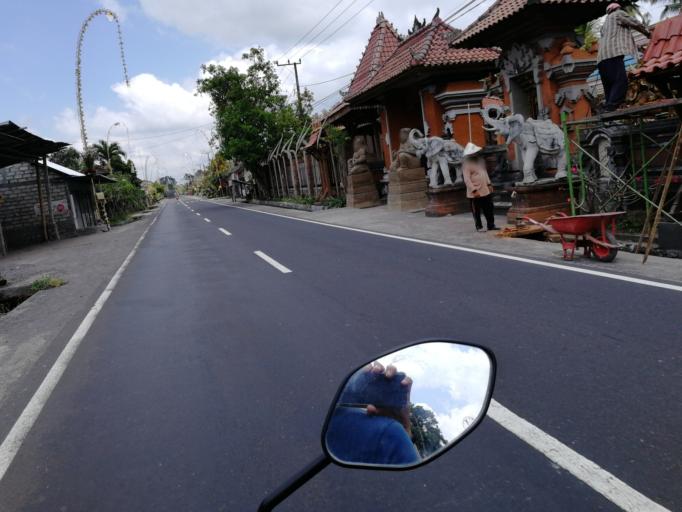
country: ID
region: Bali
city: Banjar Kubu
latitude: -8.4286
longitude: 115.4281
